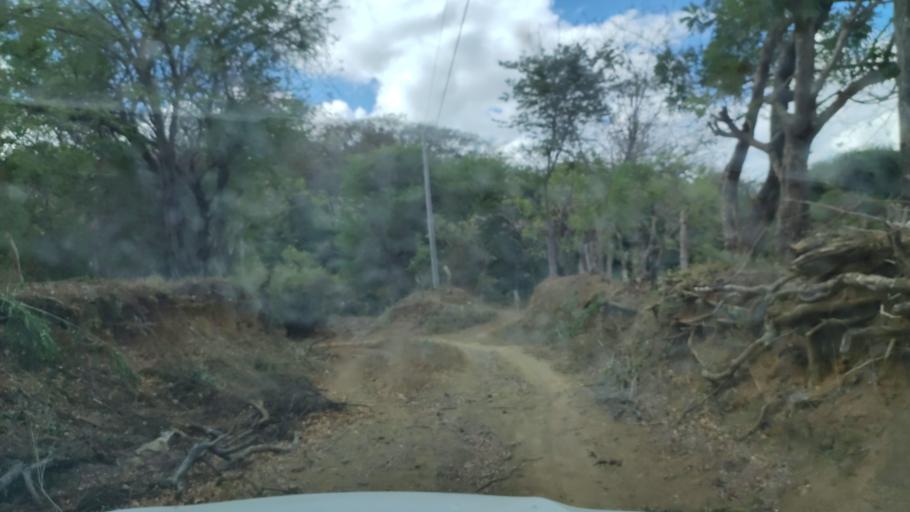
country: NI
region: Carazo
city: Santa Teresa
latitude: 11.6345
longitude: -86.2251
